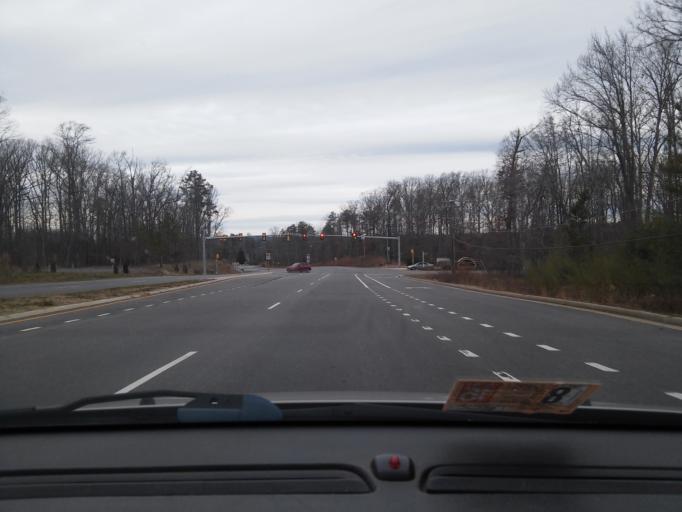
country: US
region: Virginia
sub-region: Chesterfield County
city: Bon Air
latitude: 37.5465
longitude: -77.6526
